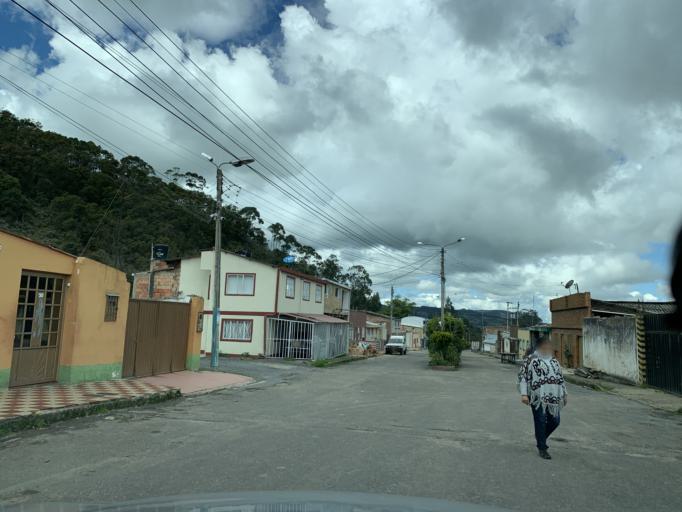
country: CO
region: Boyaca
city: Arcabuco
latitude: 5.7537
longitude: -73.4378
